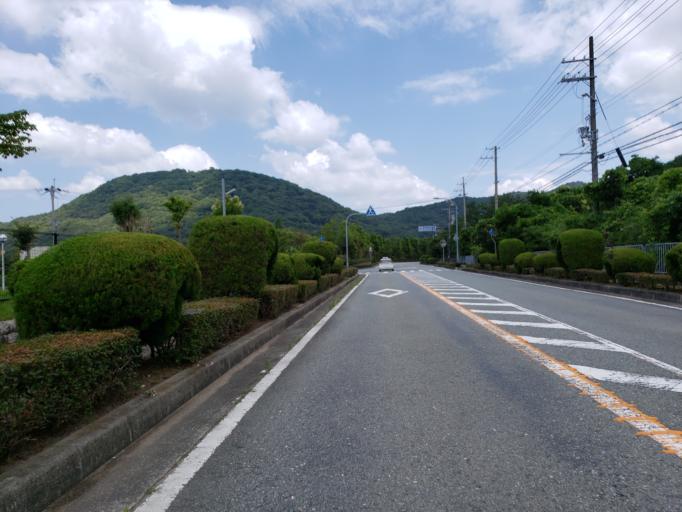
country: JP
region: Hyogo
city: Aioi
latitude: 34.7824
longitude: 134.4745
